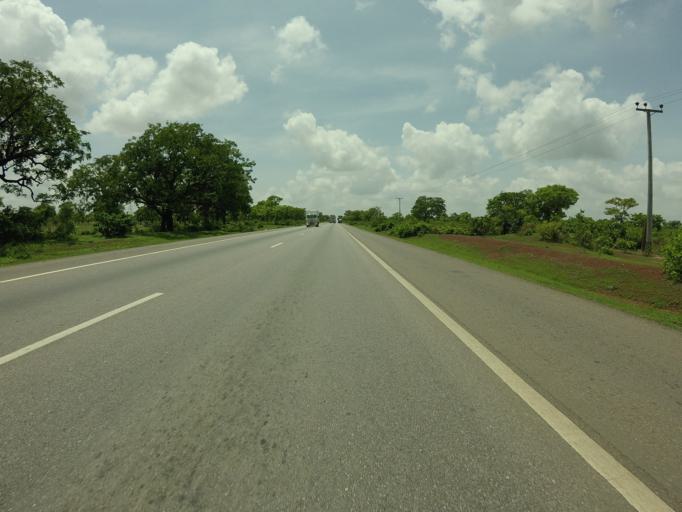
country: GH
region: Northern
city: Tamale
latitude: 9.2797
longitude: -0.9878
